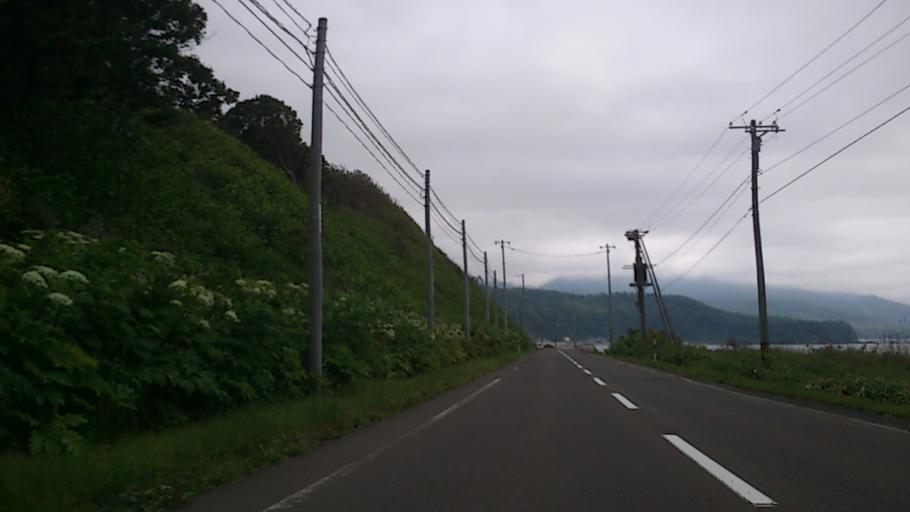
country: JP
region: Hokkaido
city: Iwanai
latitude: 42.6955
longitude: 140.0498
